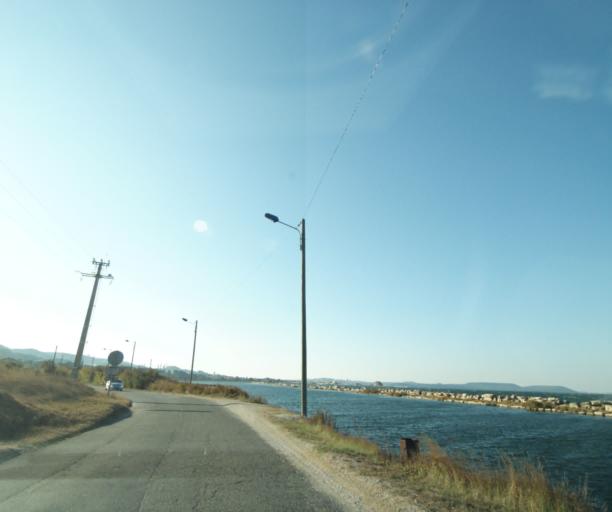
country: FR
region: Provence-Alpes-Cote d'Azur
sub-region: Departement des Bouches-du-Rhone
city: Chateauneuf-les-Martigues
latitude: 43.3994
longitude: 5.1355
